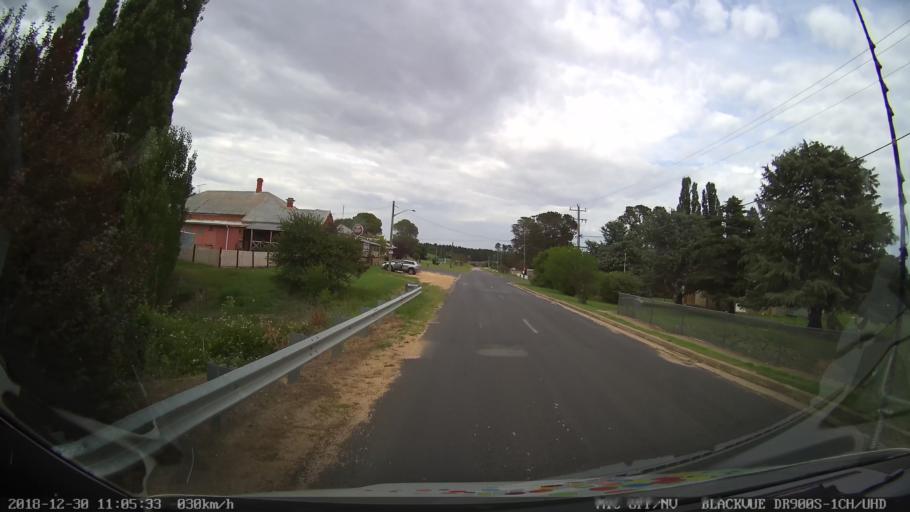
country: AU
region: New South Wales
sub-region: Snowy River
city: Berridale
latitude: -36.5034
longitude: 148.8344
